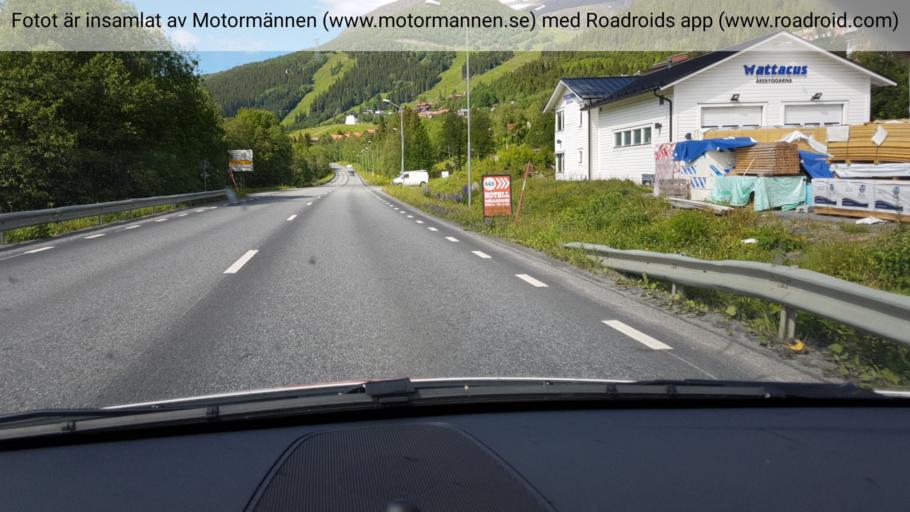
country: SE
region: Jaemtland
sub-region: Are Kommun
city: Are
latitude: 63.3921
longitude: 13.0948
